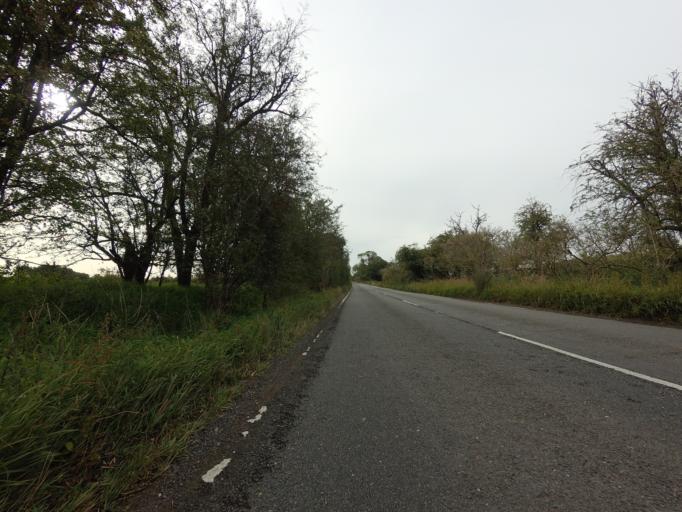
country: GB
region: England
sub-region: Cambridgeshire
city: Melbourn
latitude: 52.0384
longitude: 0.0421
